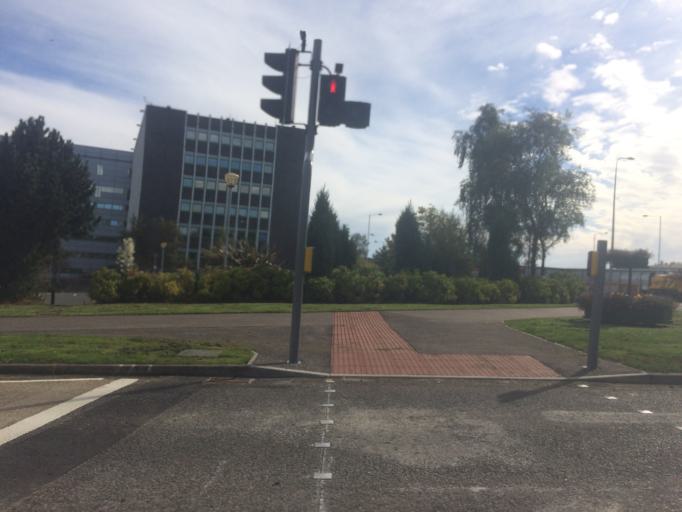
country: GB
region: Scotland
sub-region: Fife
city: Glenrothes
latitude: 56.1977
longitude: -3.1782
